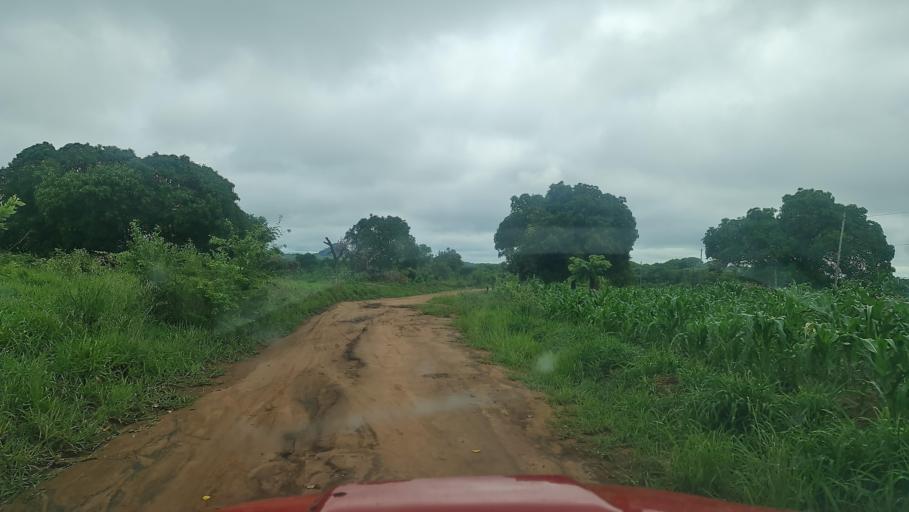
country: MW
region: Southern Region
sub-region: Nsanje District
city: Nsanje
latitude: -17.1936
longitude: 35.8481
